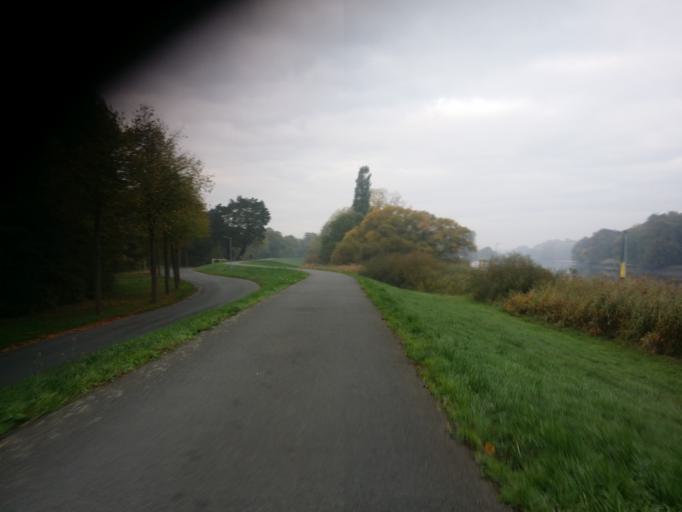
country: DE
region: Lower Saxony
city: Ritterhude
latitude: 53.1624
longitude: 8.6879
